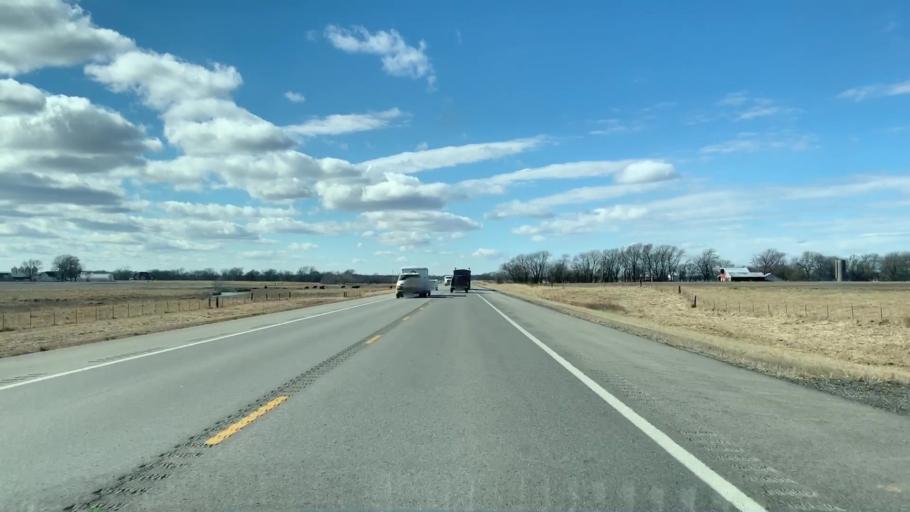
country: US
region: Kansas
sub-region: Crawford County
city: Pittsburg
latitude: 37.3396
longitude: -94.8532
